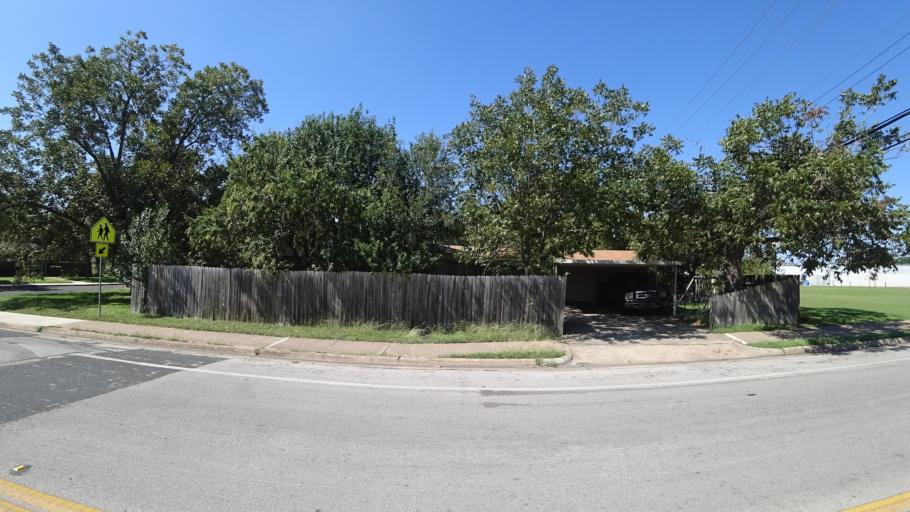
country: US
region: Texas
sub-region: Travis County
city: Austin
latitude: 30.3107
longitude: -97.6906
